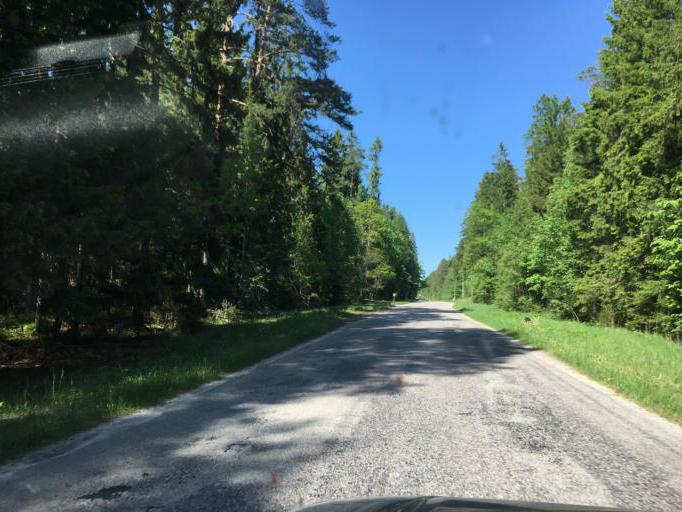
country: LV
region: Dundaga
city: Dundaga
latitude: 57.4832
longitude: 22.3395
